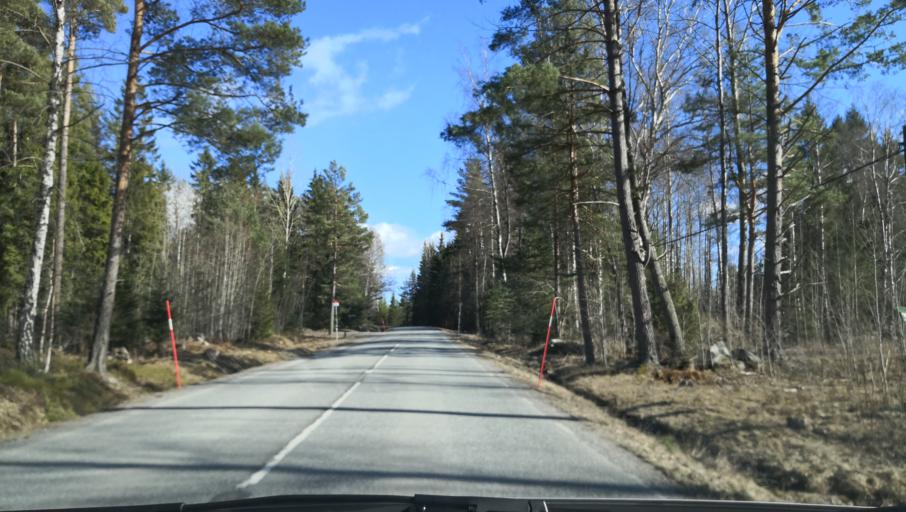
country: SE
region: Stockholm
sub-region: Varmdo Kommun
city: Holo
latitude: 59.3561
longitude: 18.5954
